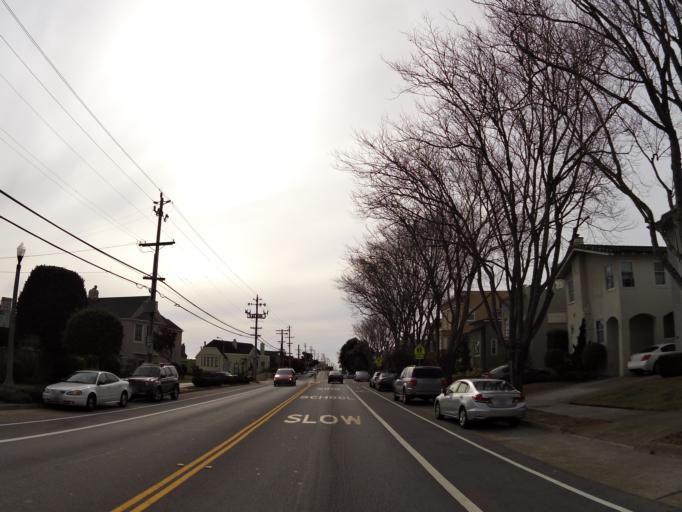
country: US
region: California
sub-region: San Mateo County
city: Daly City
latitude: 37.7437
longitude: -122.4650
